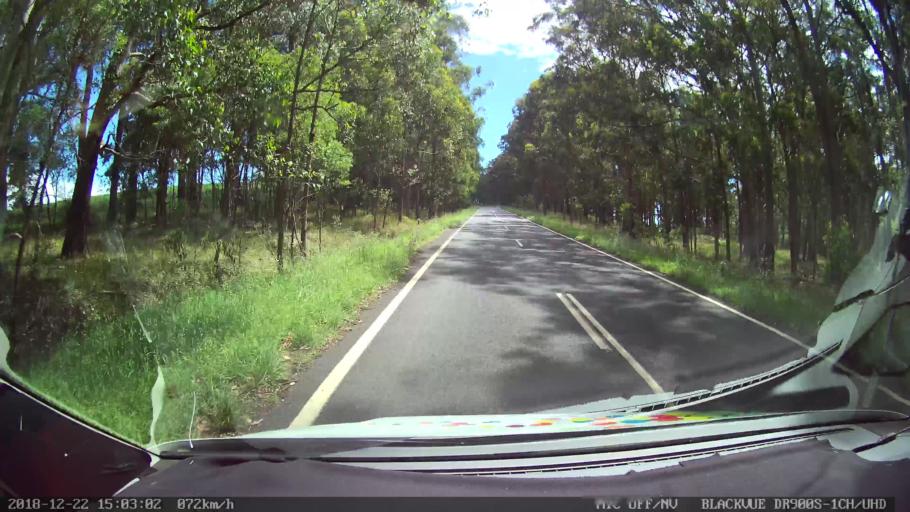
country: AU
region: New South Wales
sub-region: Bellingen
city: Dorrigo
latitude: -30.2615
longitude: 152.4443
